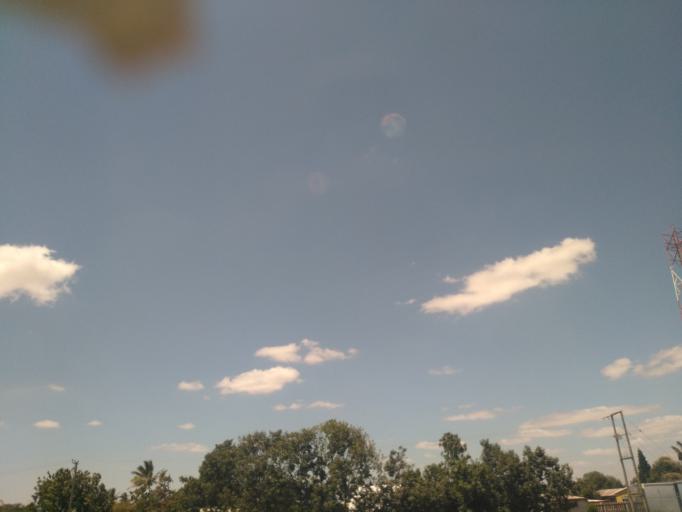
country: TZ
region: Dodoma
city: Dodoma
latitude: -6.1890
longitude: 35.7348
